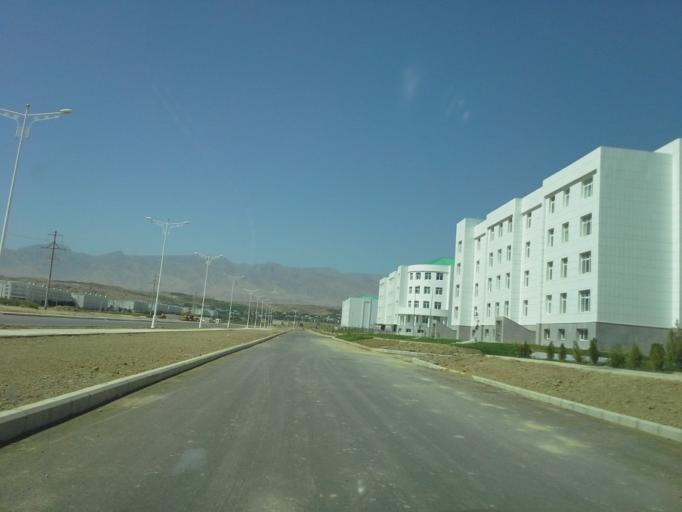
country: TM
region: Ahal
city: Ashgabat
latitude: 37.9740
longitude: 58.3310
